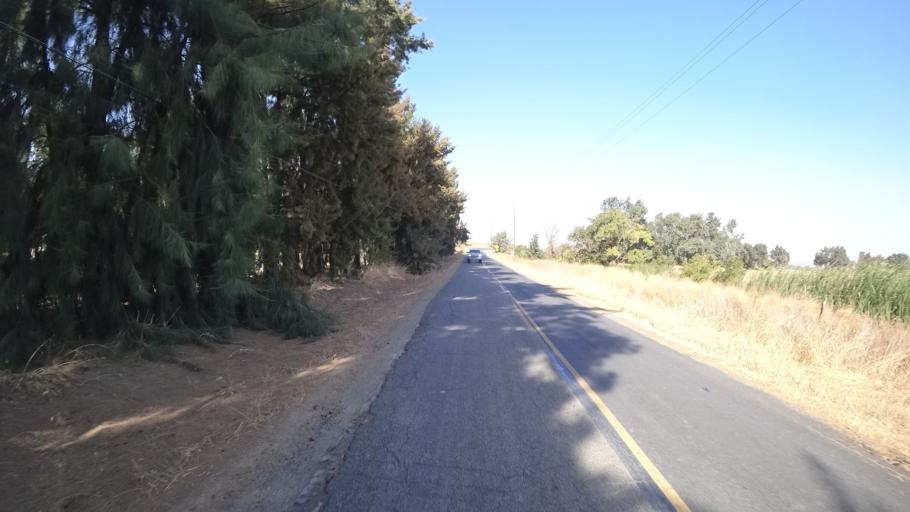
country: US
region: California
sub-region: Yolo County
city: Woodland
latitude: 38.7268
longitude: -121.8563
